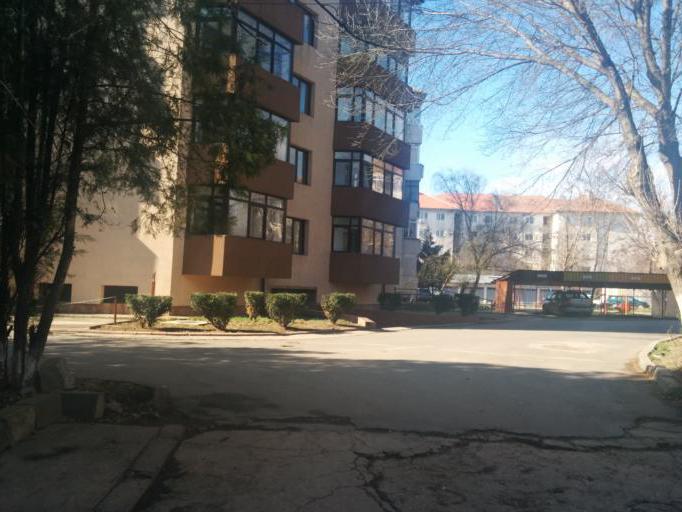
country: RO
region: Ialomita
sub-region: Comuna Slobozia
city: Slobozia
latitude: 44.5647
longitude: 27.3682
